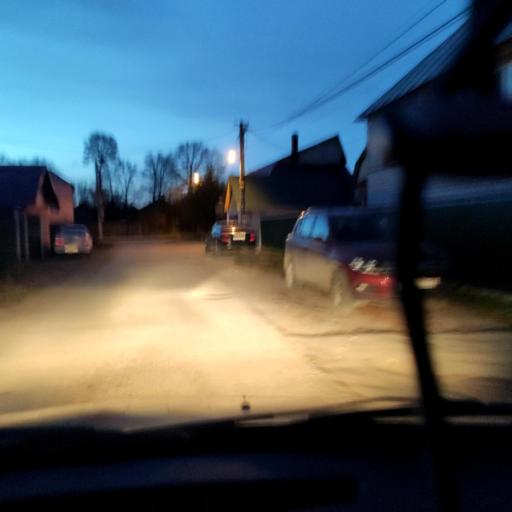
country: RU
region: Bashkortostan
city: Ufa
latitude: 54.7244
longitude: 55.9035
